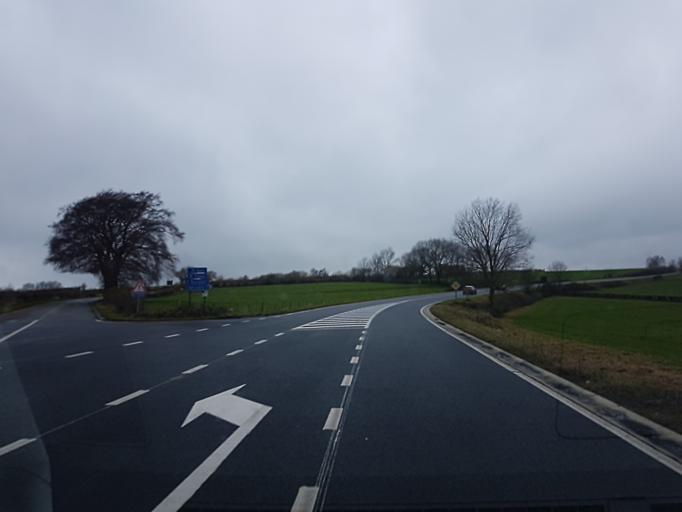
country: BE
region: Wallonia
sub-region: Province de Liege
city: Jalhay
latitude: 50.5580
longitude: 5.9460
